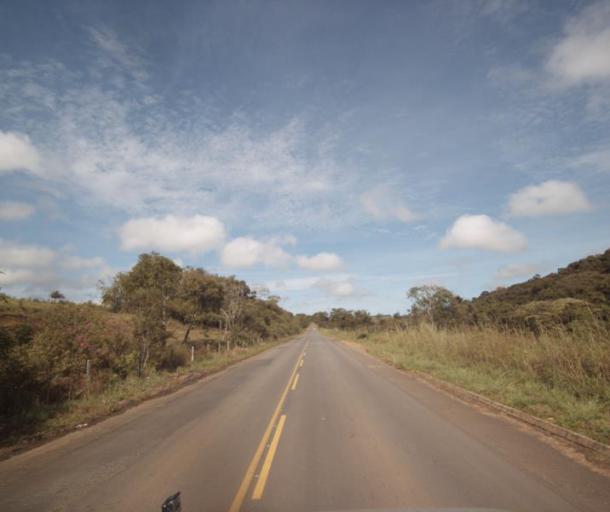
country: BR
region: Goias
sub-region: Pirenopolis
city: Pirenopolis
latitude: -15.9884
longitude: -48.8322
